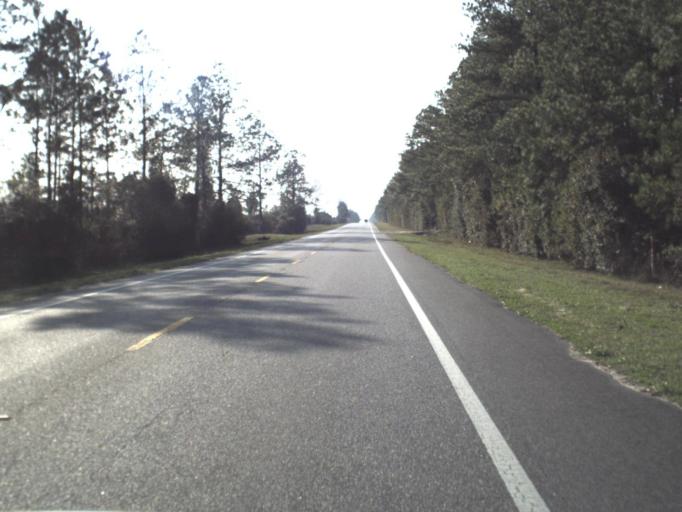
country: US
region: Florida
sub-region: Bay County
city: Lynn Haven
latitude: 30.4395
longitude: -85.7581
